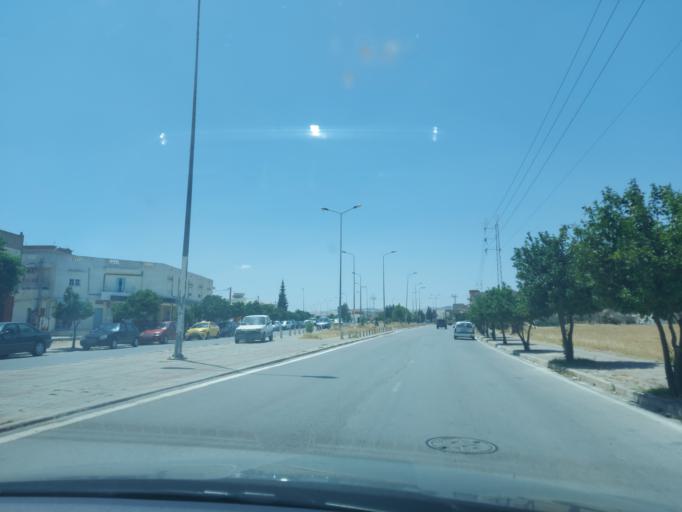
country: TN
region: Silyanah
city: Siliana
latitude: 36.0853
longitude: 9.3575
